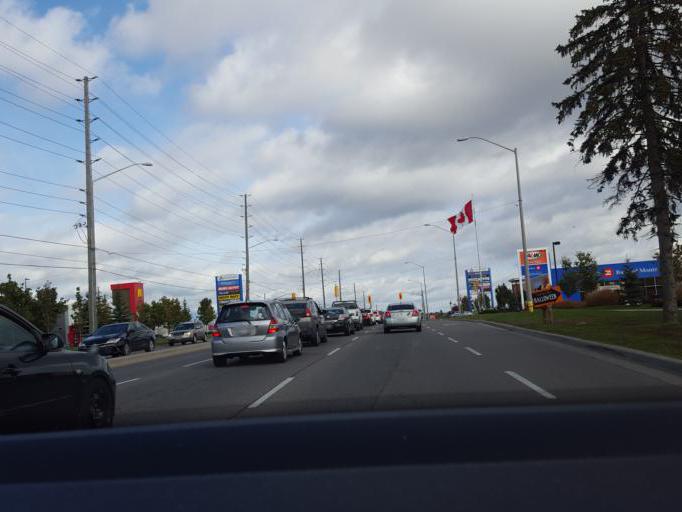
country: CA
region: Ontario
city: Oshawa
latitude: 43.9401
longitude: -78.8469
